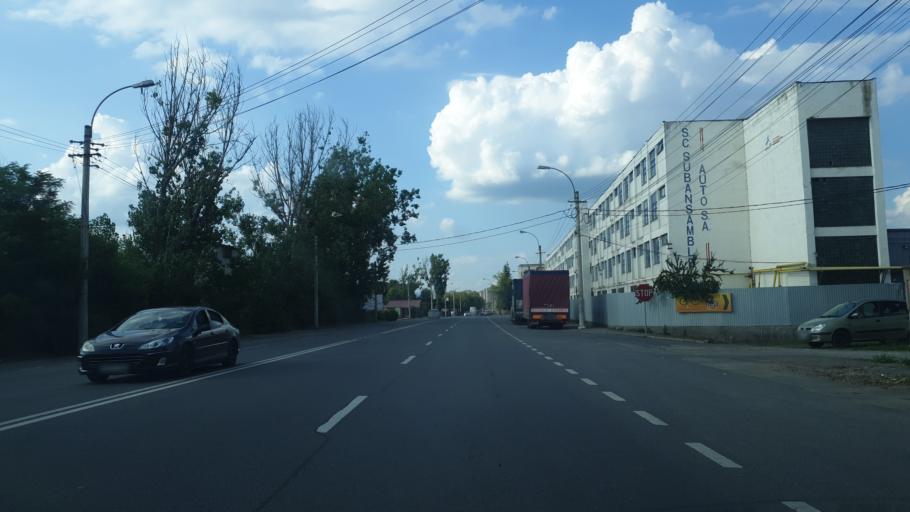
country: RO
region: Covasna
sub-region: Municipiul Sfantu Gheorghe
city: Sfantu-Gheorghe
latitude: 45.8500
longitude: 25.8057
